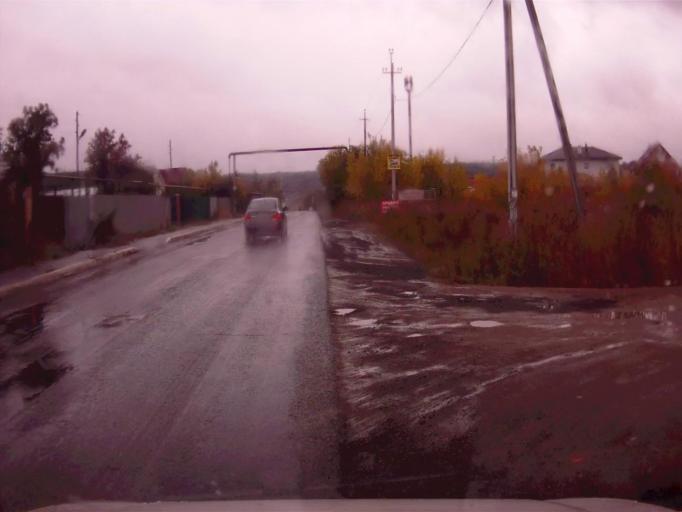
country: RU
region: Chelyabinsk
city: Dolgoderevenskoye
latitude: 55.3095
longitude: 61.3411
